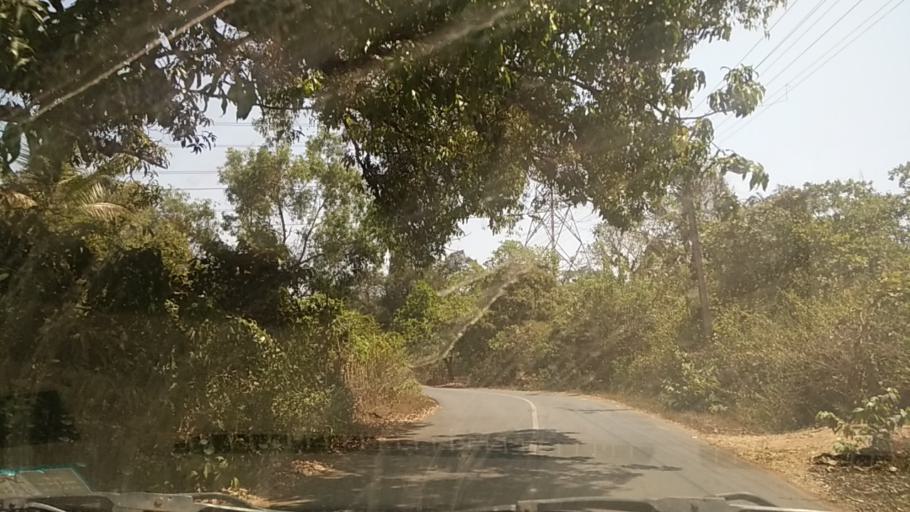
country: IN
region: Goa
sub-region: North Goa
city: Dicholi
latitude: 15.5752
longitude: 73.9118
